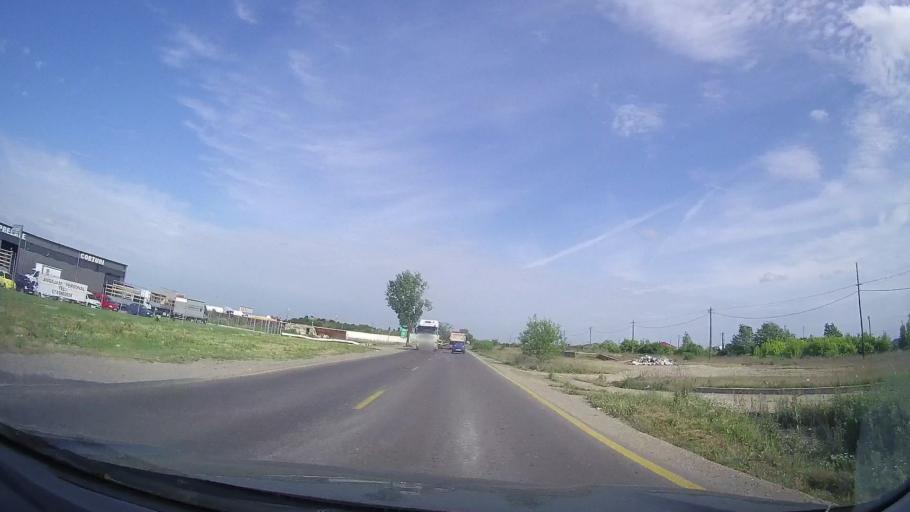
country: RO
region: Ilfov
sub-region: Comuna Magurele
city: Varteju
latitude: 44.3706
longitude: 26.0116
